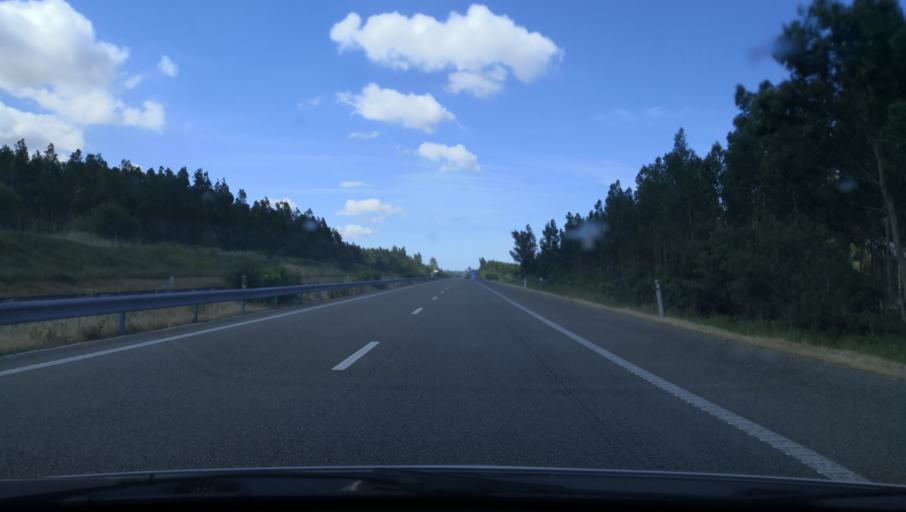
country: PT
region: Coimbra
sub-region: Montemor-O-Velho
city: Montemor-o-Velho
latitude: 40.1857
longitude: -8.7018
